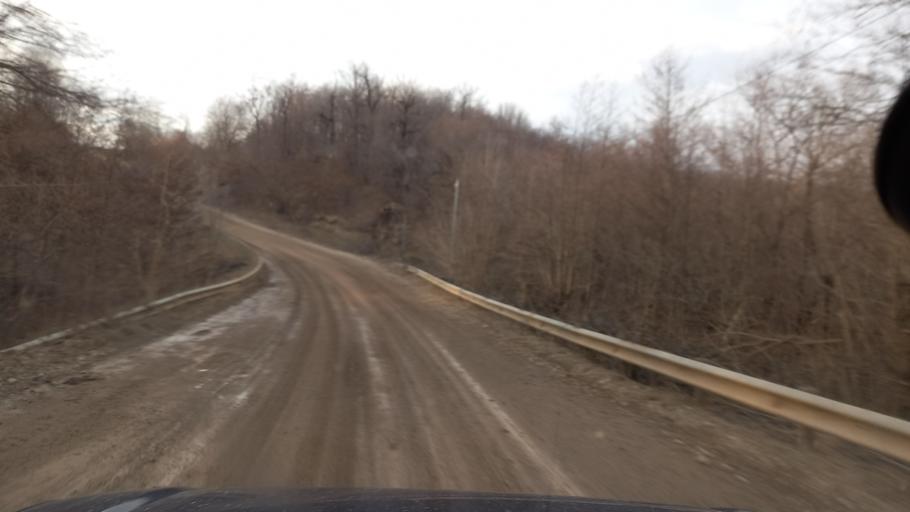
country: RU
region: Adygeya
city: Kamennomostskiy
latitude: 44.1930
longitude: 40.2588
